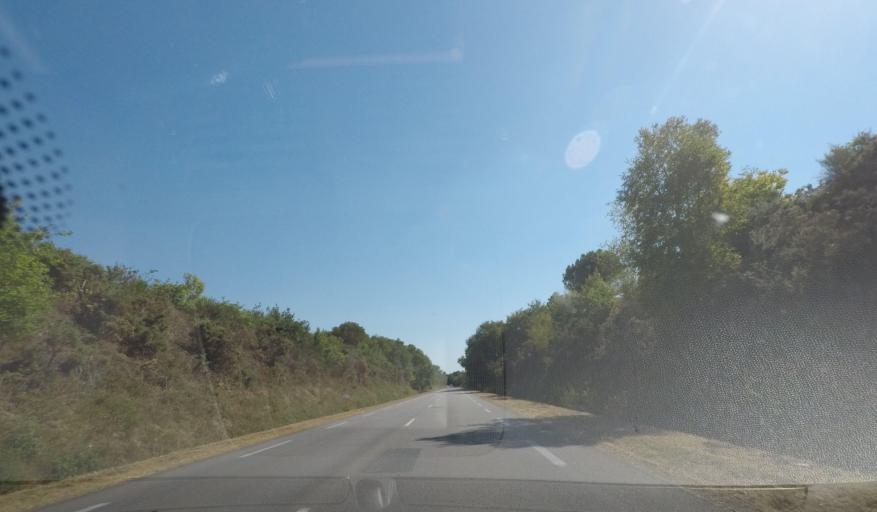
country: FR
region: Brittany
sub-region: Departement du Morbihan
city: Questembert
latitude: 47.6582
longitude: -2.4282
